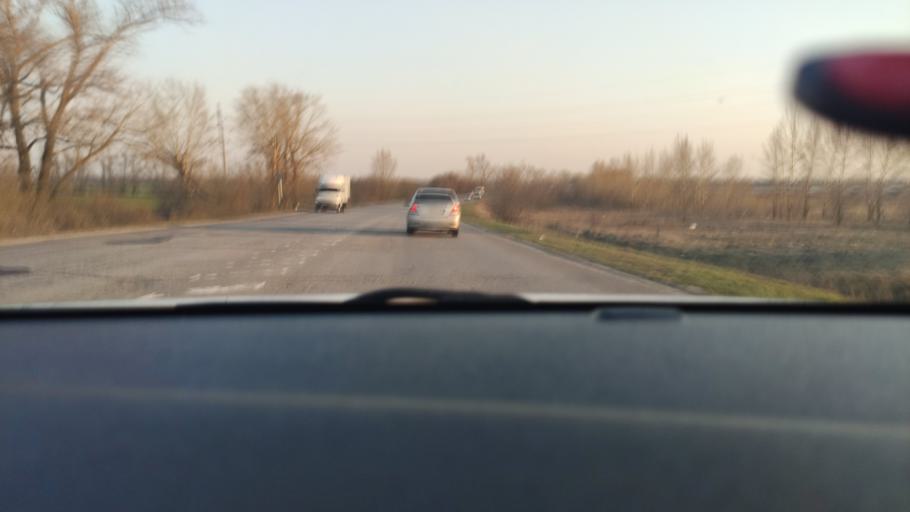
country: RU
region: Voronezj
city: Maslovka
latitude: 51.5030
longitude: 39.3085
